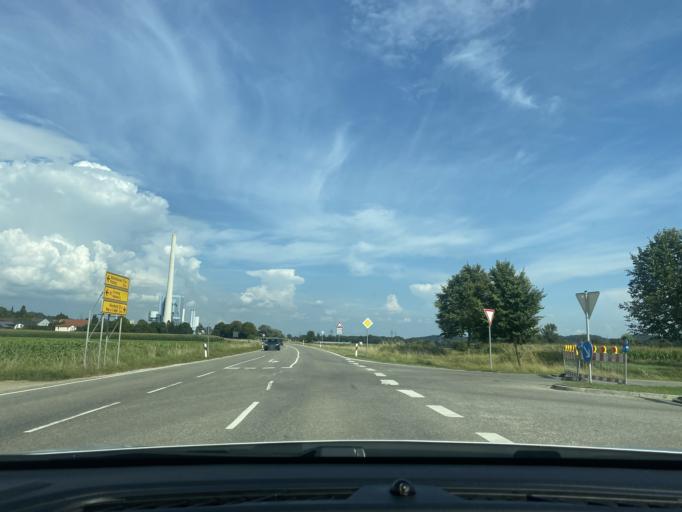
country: DE
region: Bavaria
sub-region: Upper Bavaria
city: Zolling
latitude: 48.4534
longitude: 11.7840
